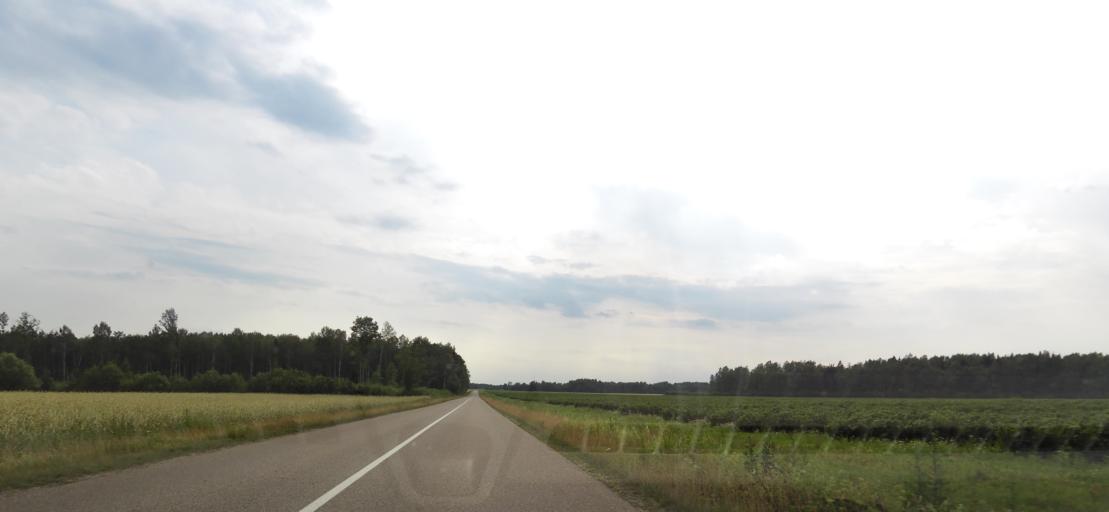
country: LT
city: Obeliai
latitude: 56.1125
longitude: 25.0736
